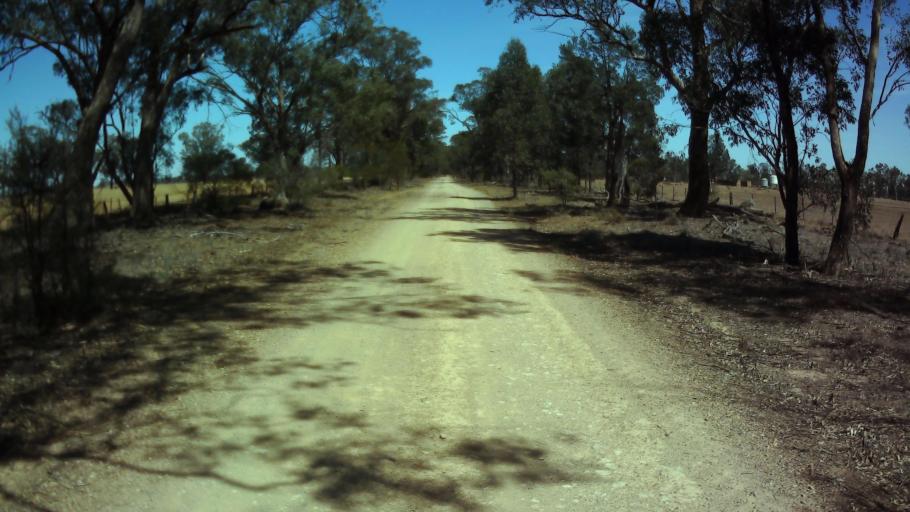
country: AU
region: New South Wales
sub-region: Weddin
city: Grenfell
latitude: -34.0687
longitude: 147.8941
